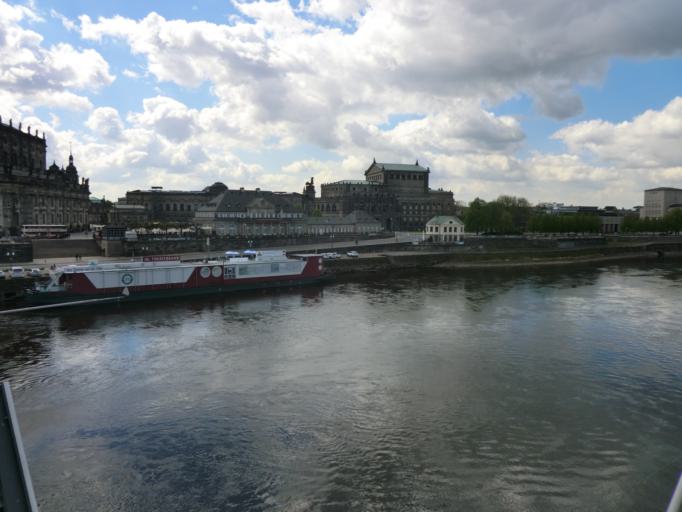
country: DE
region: Saxony
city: Dresden
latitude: 51.0552
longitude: 13.7394
